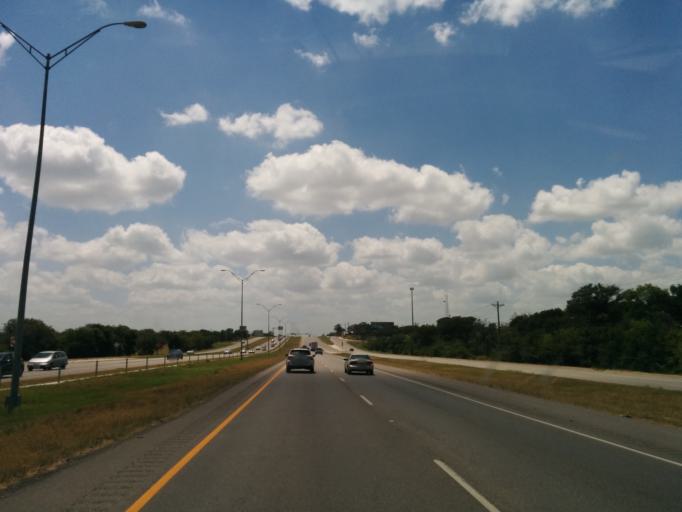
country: US
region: Texas
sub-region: Bastrop County
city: Bastrop
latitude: 30.1112
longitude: -97.3596
